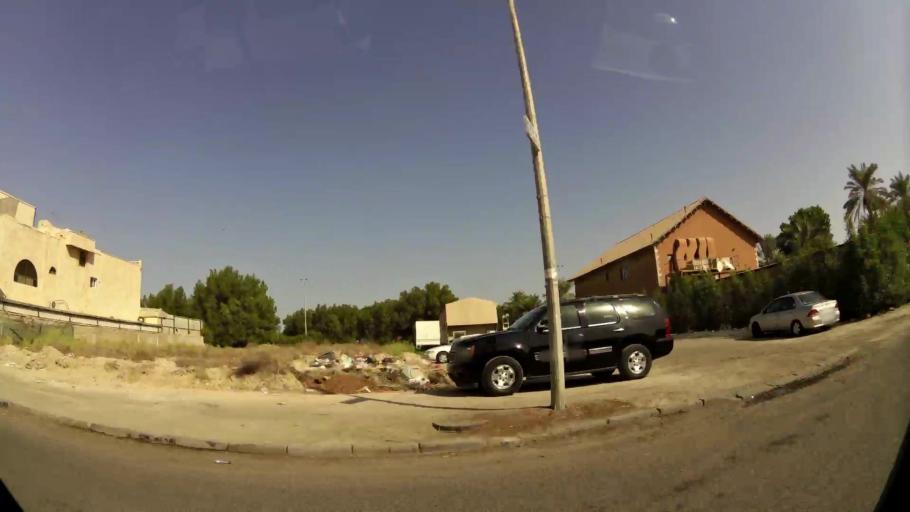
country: KW
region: Muhafazat Hawalli
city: Salwa
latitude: 29.2889
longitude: 48.0850
